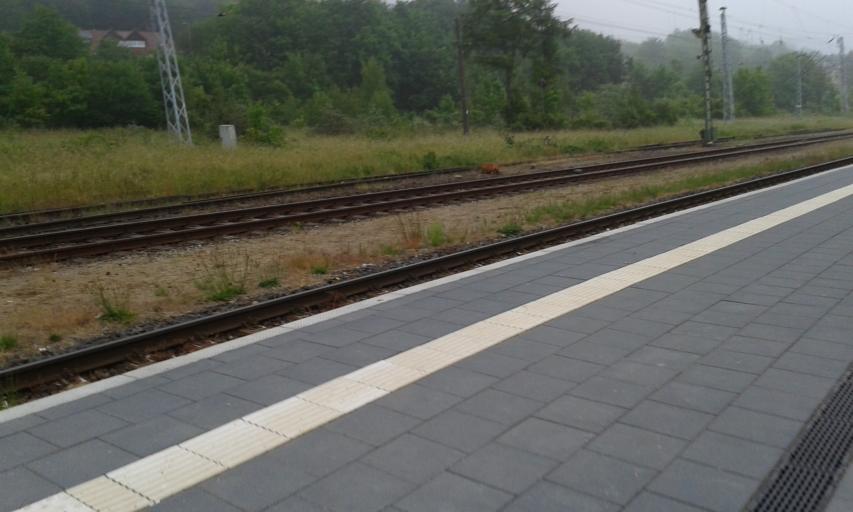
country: DE
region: Mecklenburg-Vorpommern
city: Sassnitz
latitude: 54.5163
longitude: 13.6377
